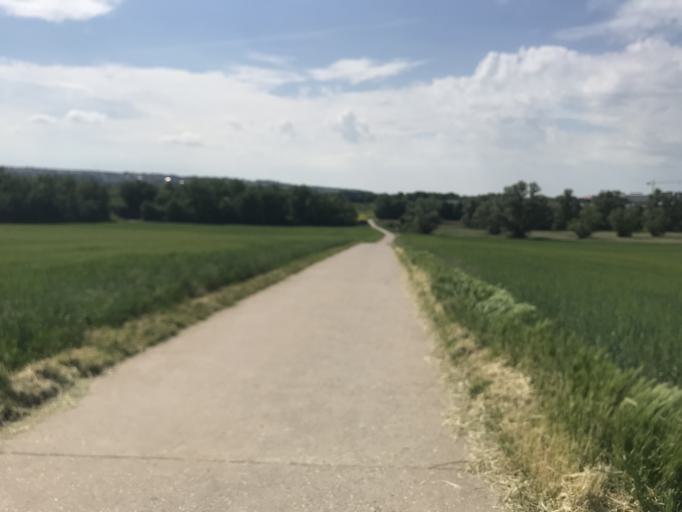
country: DE
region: Rheinland-Pfalz
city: Nieder-Olm
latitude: 49.9188
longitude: 8.1913
